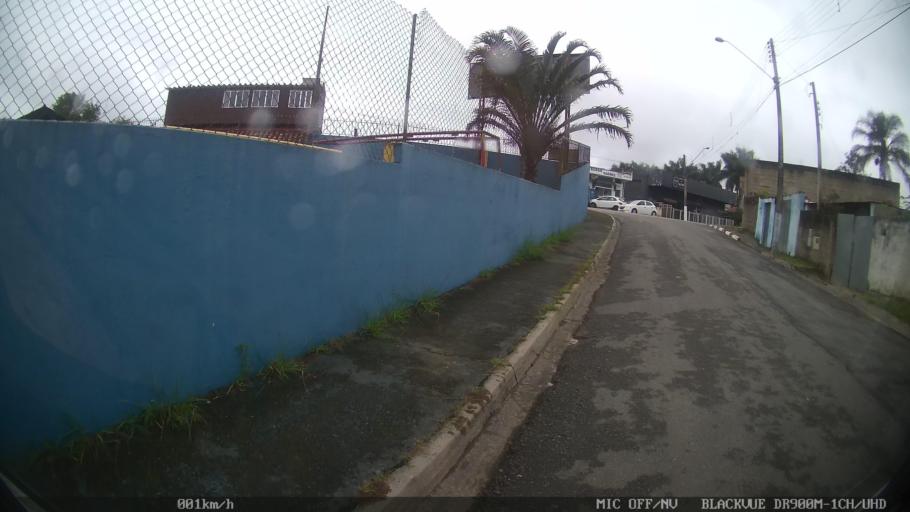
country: BR
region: Sao Paulo
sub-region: Juquia
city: Juquia
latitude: -24.3253
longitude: -47.6312
